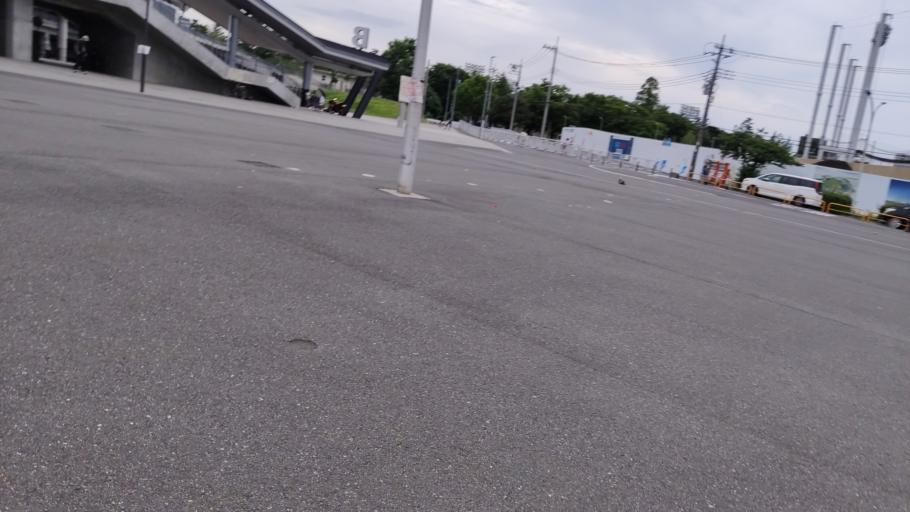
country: JP
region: Kanagawa
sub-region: Kawasaki-shi
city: Kawasaki
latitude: 35.5865
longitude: 139.6512
